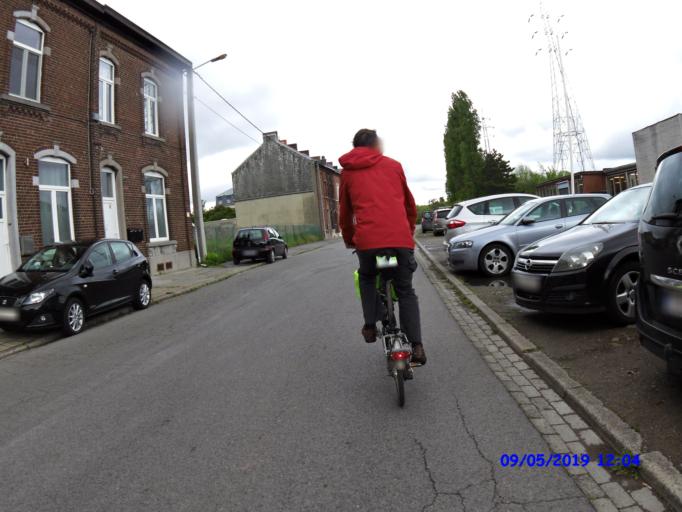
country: BE
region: Wallonia
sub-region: Province du Hainaut
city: Chatelet
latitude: 50.3996
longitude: 4.4860
